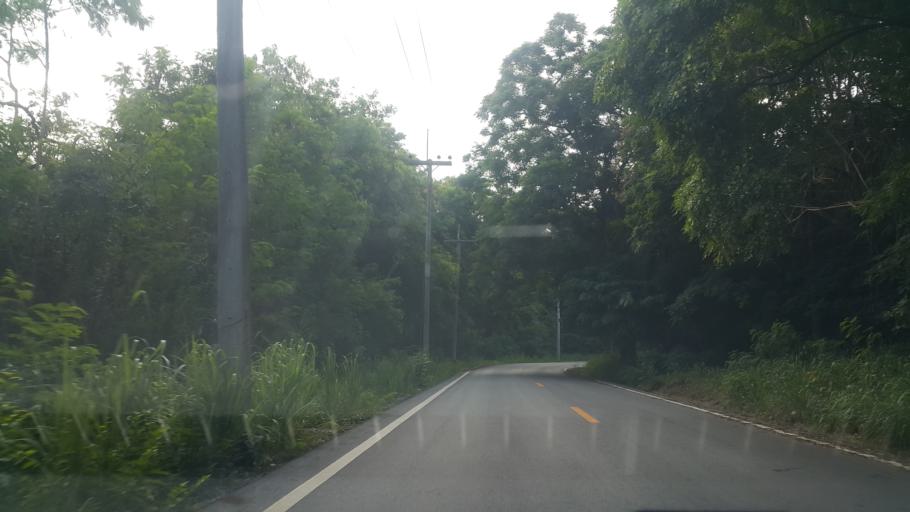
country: TH
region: Rayong
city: Ban Chang
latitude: 12.7825
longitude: 100.9651
